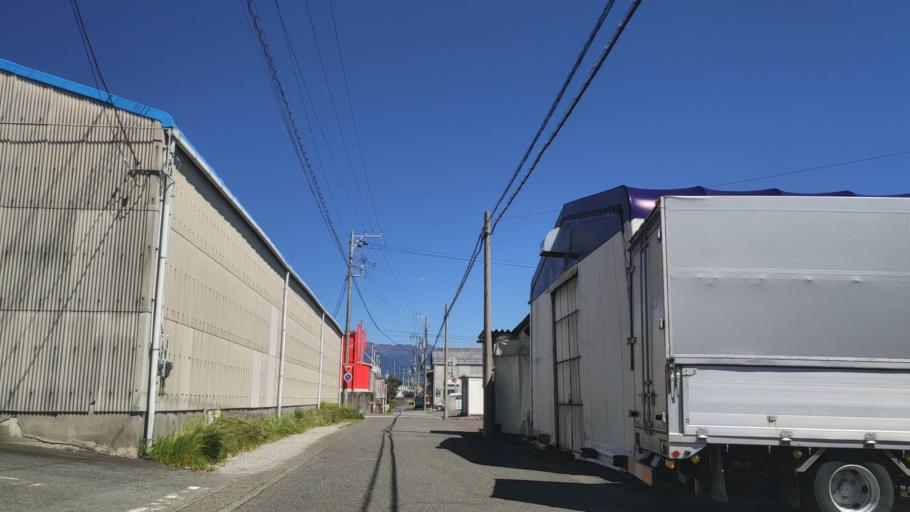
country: JP
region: Shizuoka
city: Fuji
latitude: 35.1340
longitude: 138.6515
